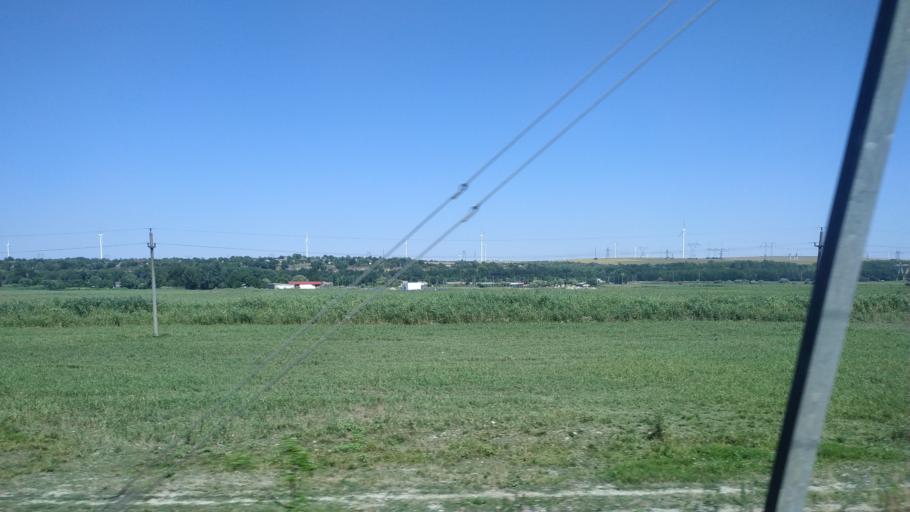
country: RO
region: Constanta
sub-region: Comuna Saligny
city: Faclia
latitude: 44.2714
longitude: 28.1114
